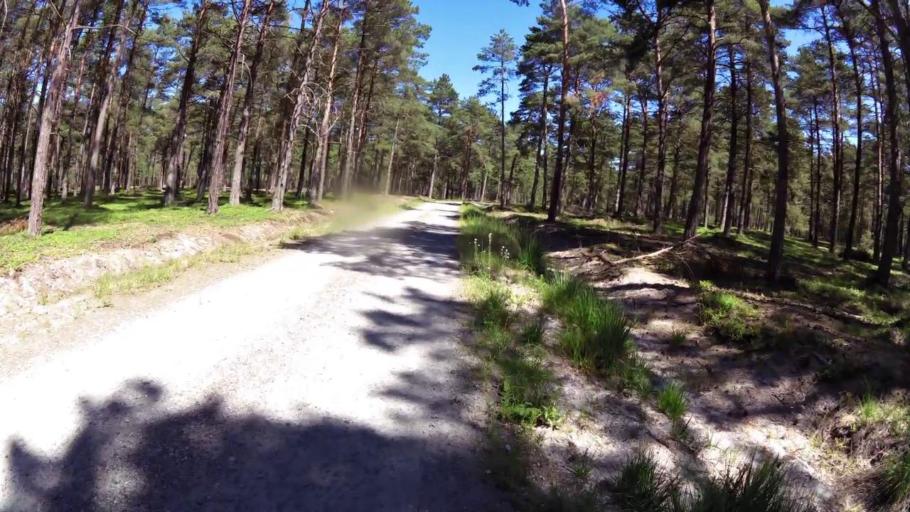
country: PL
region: West Pomeranian Voivodeship
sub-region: Powiat gryficki
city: Cerkwica
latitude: 54.0988
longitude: 15.1562
